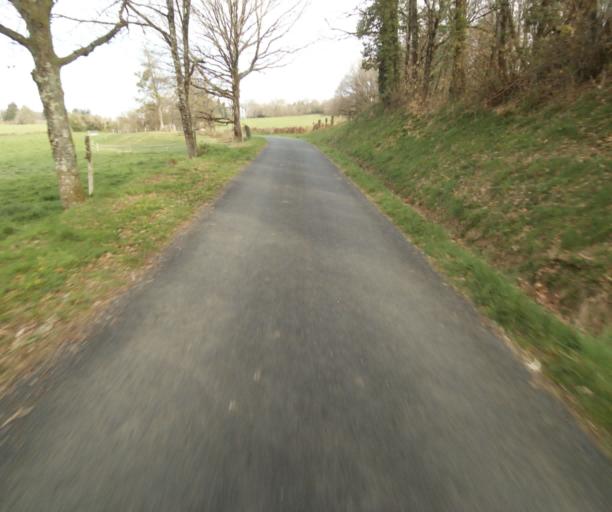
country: FR
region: Limousin
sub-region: Departement de la Correze
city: Chamboulive
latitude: 45.4482
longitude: 1.7546
